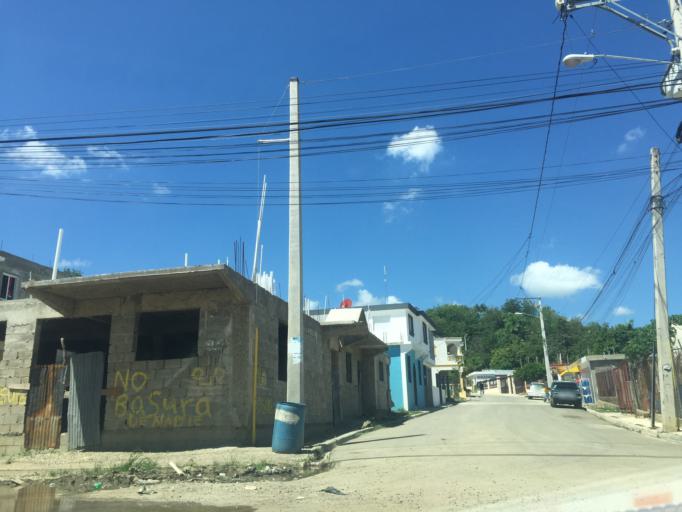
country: DO
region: Santiago
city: Santiago de los Caballeros
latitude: 19.4417
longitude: -70.7443
